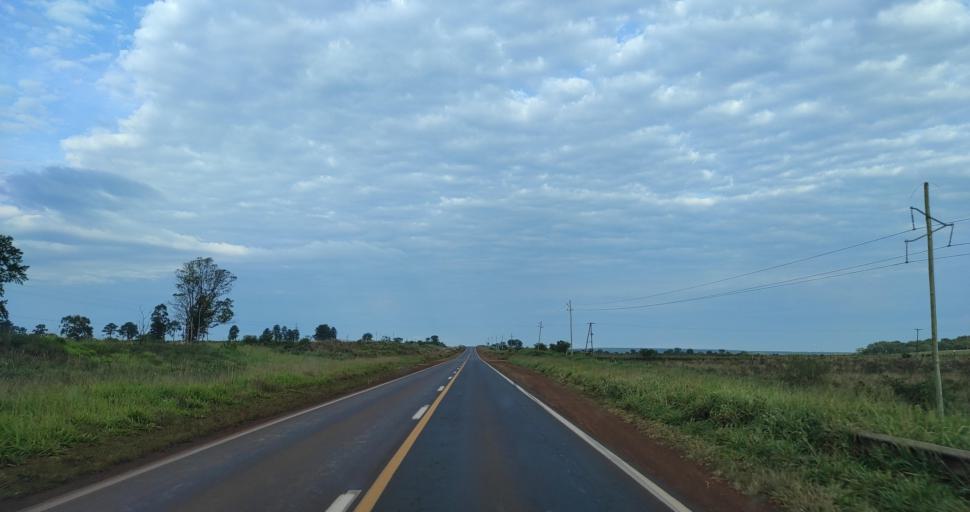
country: AR
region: Corrientes
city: San Carlos
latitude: -27.9039
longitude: -55.9448
